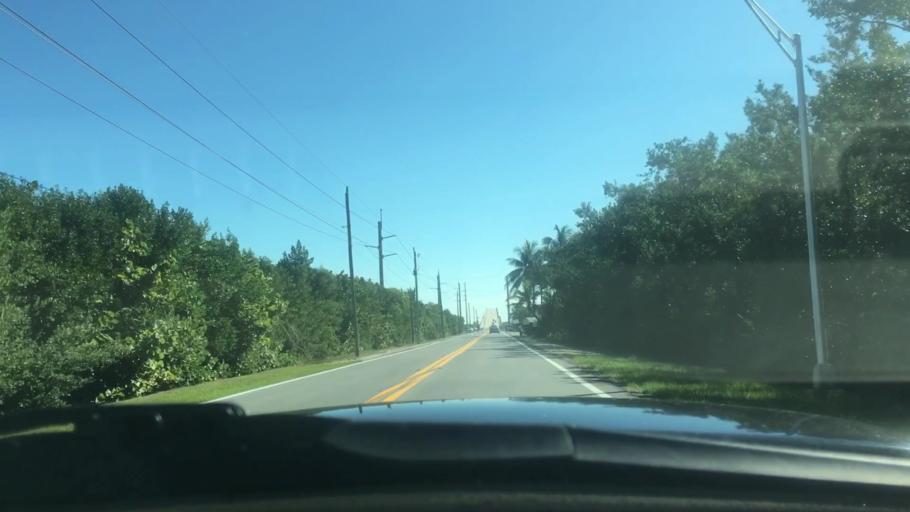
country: US
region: Florida
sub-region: Monroe County
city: North Key Largo
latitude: 25.2906
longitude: -80.3765
